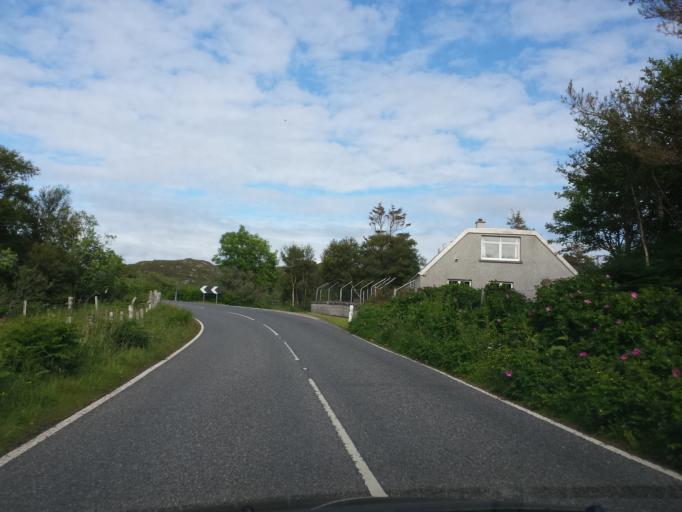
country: GB
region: Scotland
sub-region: Argyll and Bute
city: Isle Of Mull
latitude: 56.9495
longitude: -5.8487
